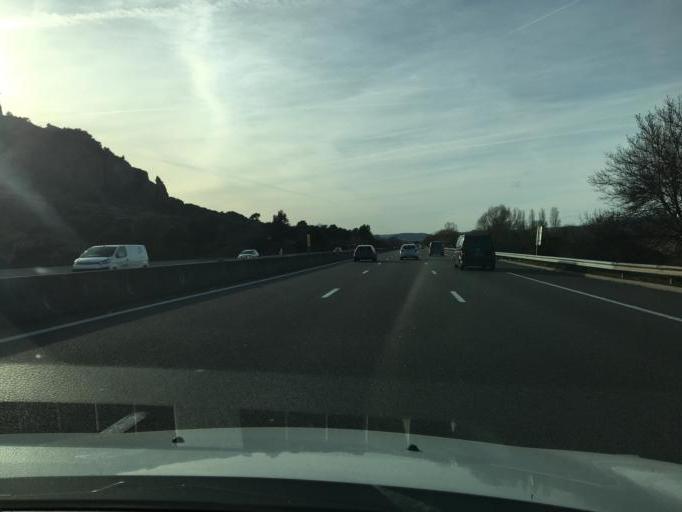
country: FR
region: Provence-Alpes-Cote d'Azur
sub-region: Departement du Var
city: Le Muy
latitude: 43.4592
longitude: 6.6008
